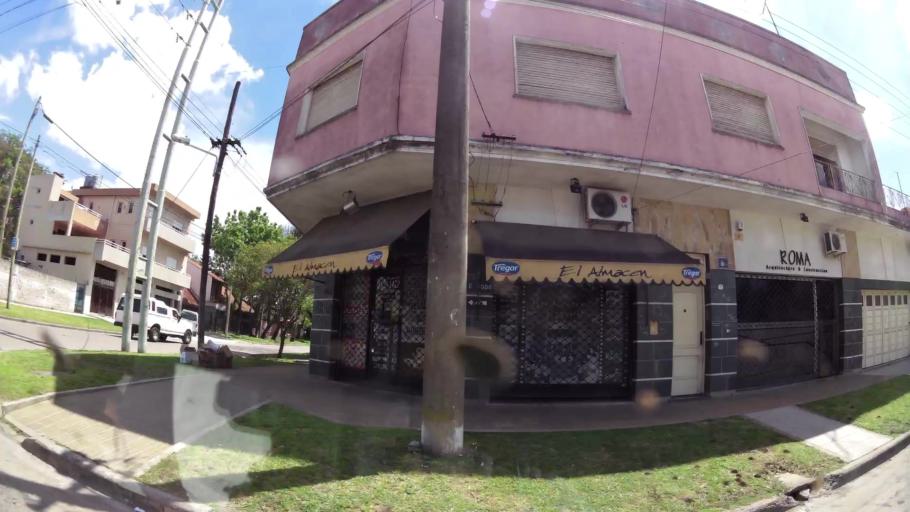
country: AR
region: Buenos Aires
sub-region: Partido de Quilmes
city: Quilmes
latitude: -34.8084
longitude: -58.2683
